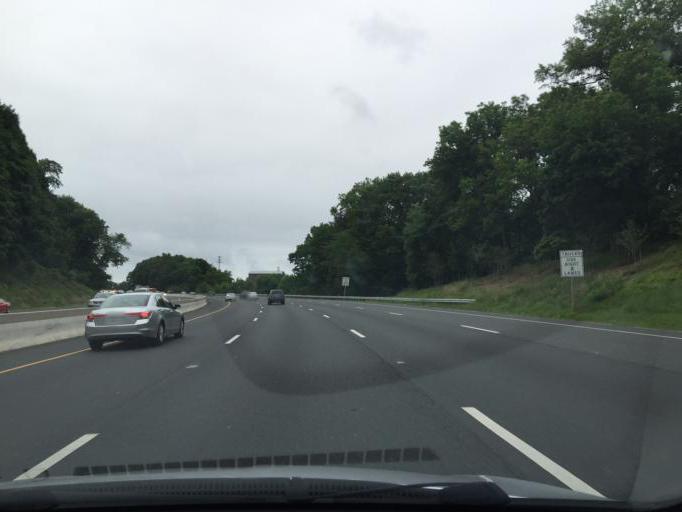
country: US
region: Maryland
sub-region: Baltimore County
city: Lutherville
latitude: 39.3741
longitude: -76.6538
